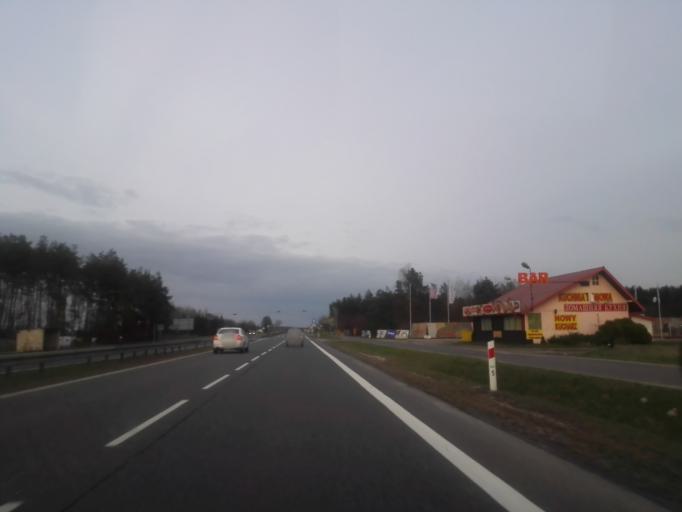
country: PL
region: Masovian Voivodeship
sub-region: Powiat zyrardowski
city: Radziejowice
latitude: 52.0040
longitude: 20.5792
